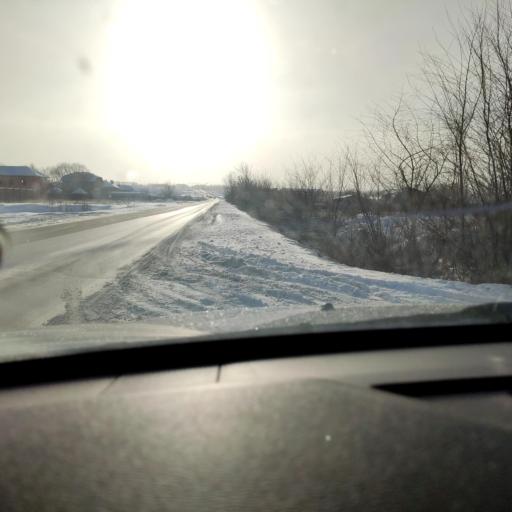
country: RU
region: Samara
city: Smyshlyayevka
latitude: 53.1588
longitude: 50.3853
